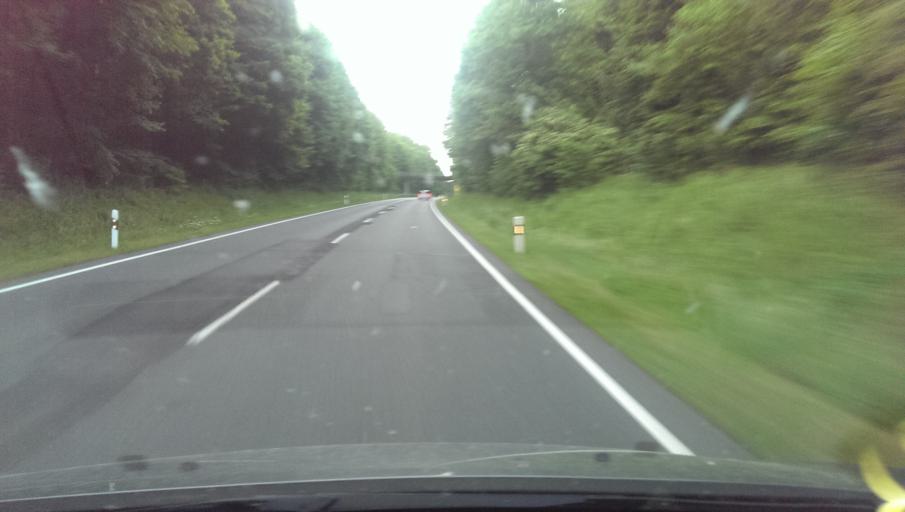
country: DE
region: Bavaria
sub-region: Regierungsbezirk Unterfranken
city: Waldbuttelbrunn
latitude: 49.7870
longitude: 9.8591
